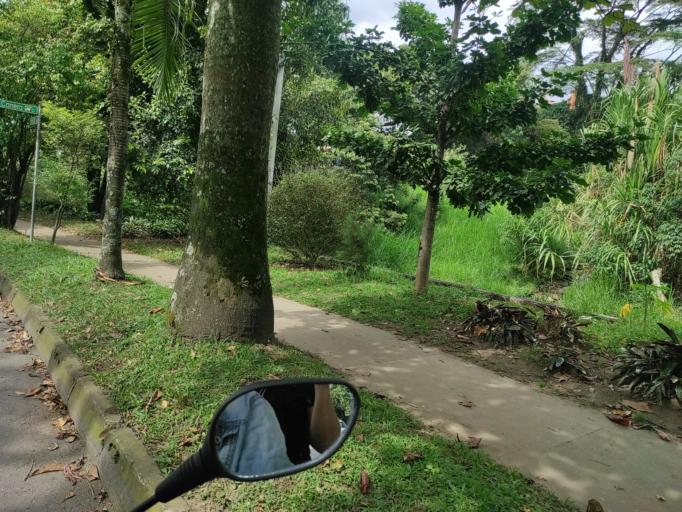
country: CO
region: Antioquia
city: Envigado
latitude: 6.1605
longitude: -75.5791
